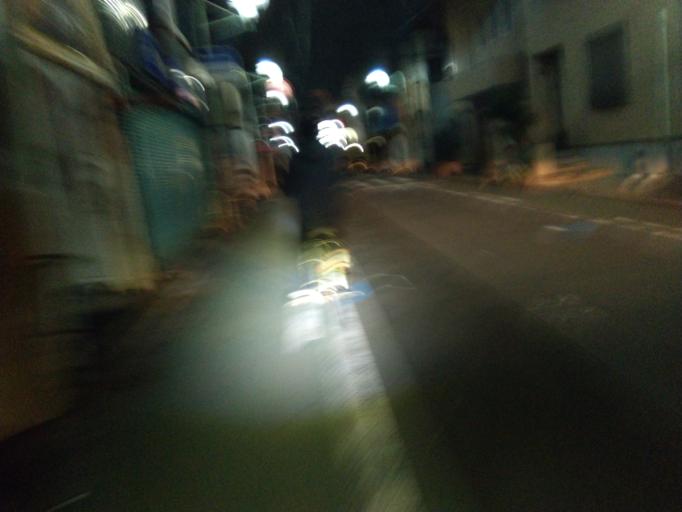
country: JP
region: Kanagawa
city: Hiratsuka
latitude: 35.3336
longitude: 139.3507
